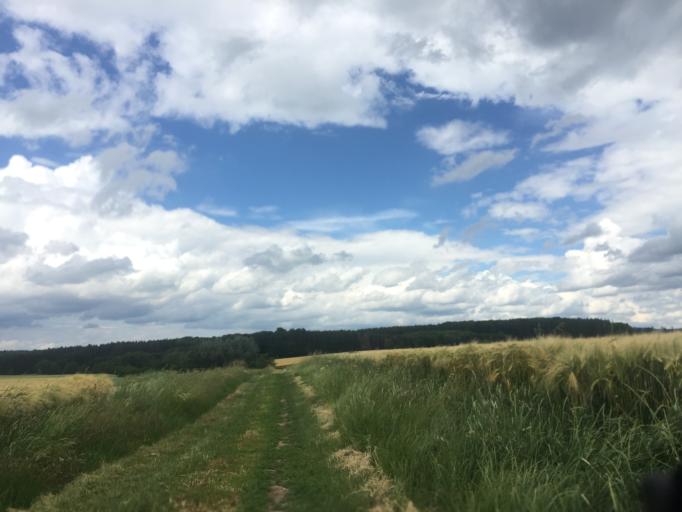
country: DE
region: Rheinland-Pfalz
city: Girod
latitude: 50.4595
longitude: 7.9162
